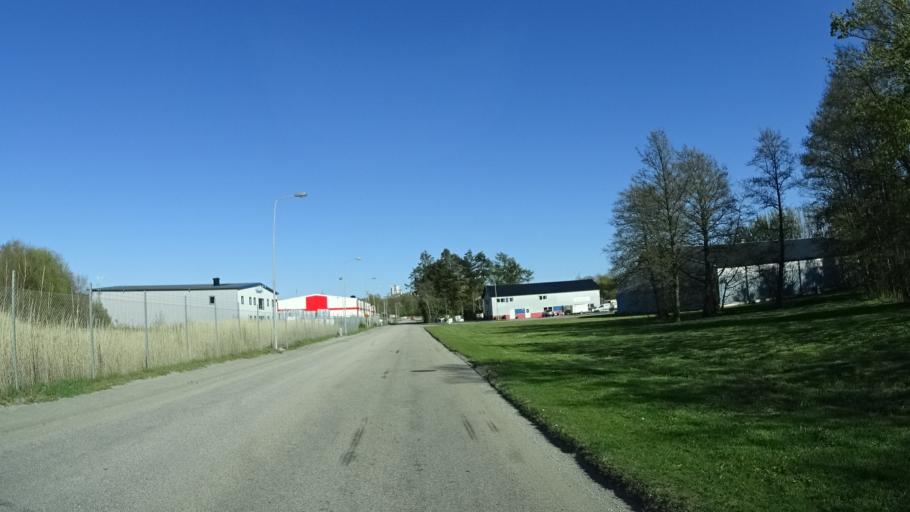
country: SE
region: Vaestra Goetaland
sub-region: Stenungsunds Kommun
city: Stenungsund
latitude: 58.0784
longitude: 11.8233
